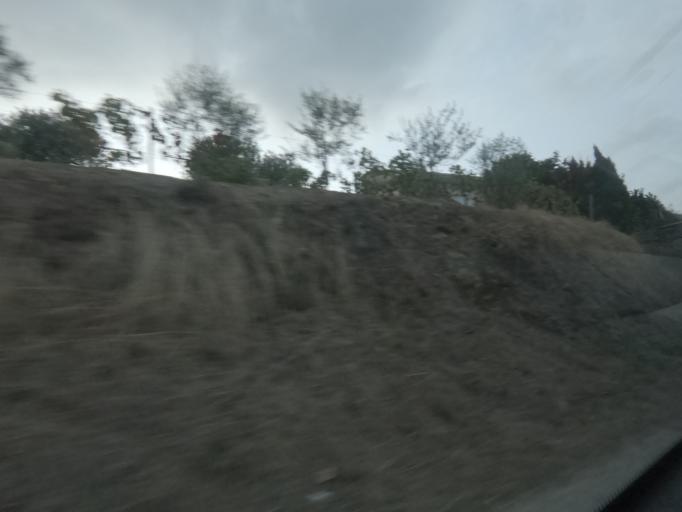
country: PT
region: Vila Real
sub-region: Peso da Regua
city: Peso da Regua
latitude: 41.1300
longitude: -7.7494
